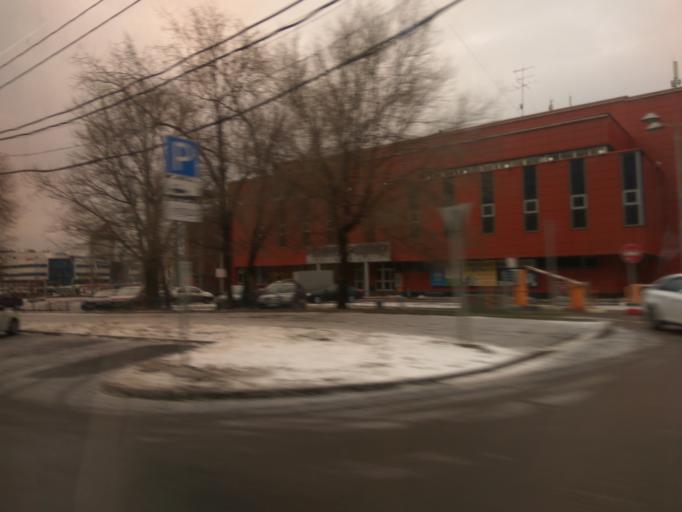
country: RU
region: Moscow
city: Orekhovo-Borisovo
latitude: 55.6133
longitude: 37.7210
